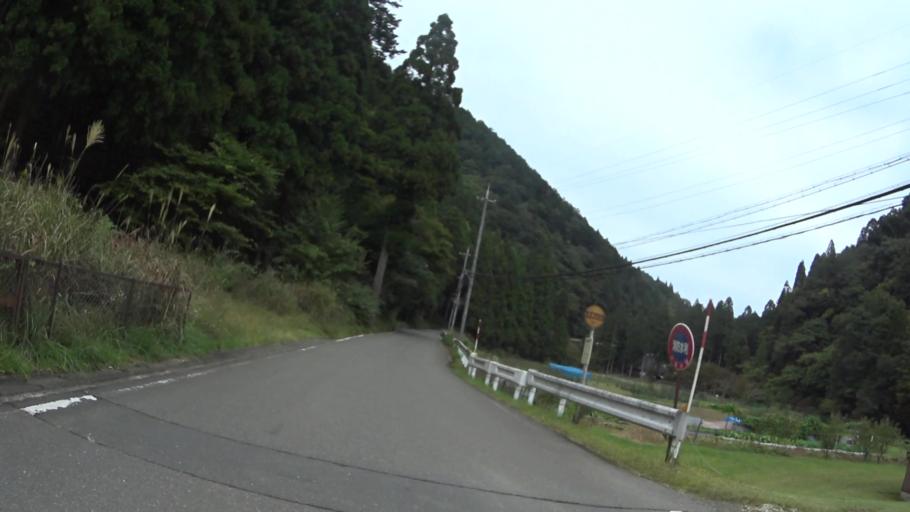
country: JP
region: Shiga Prefecture
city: Kitahama
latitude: 35.2118
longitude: 135.7763
